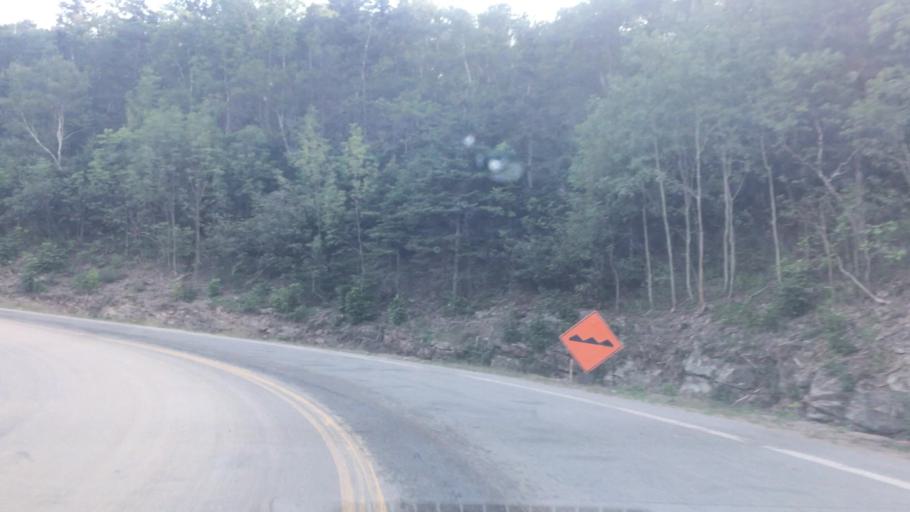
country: CA
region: Nova Scotia
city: Sydney Mines
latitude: 46.8197
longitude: -60.8368
